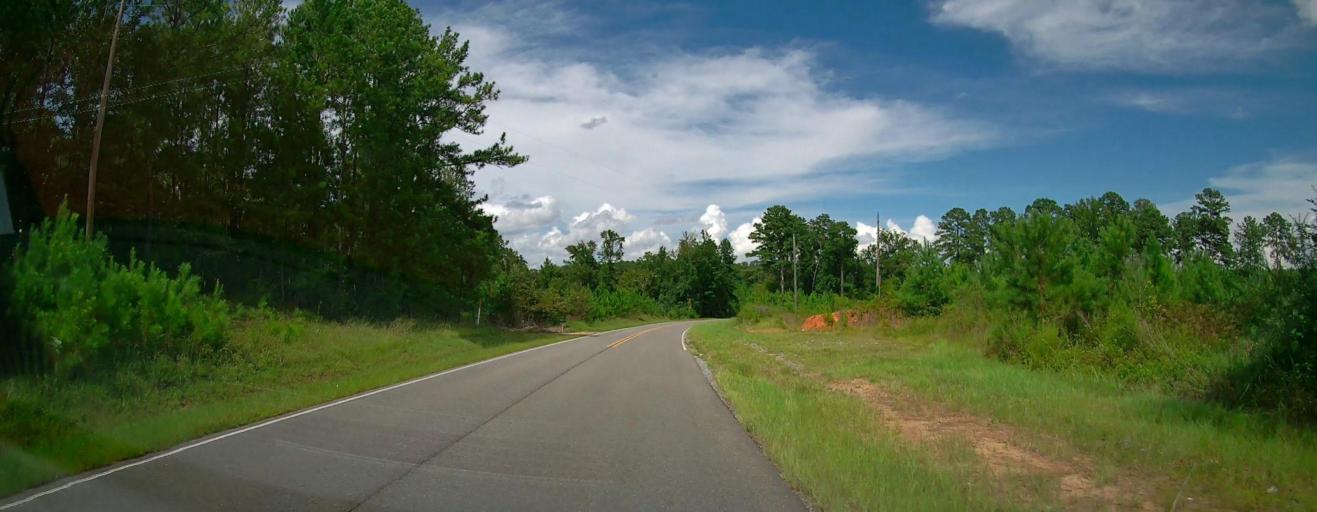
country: US
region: Georgia
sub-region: Taylor County
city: Butler
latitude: 32.4933
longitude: -84.2056
